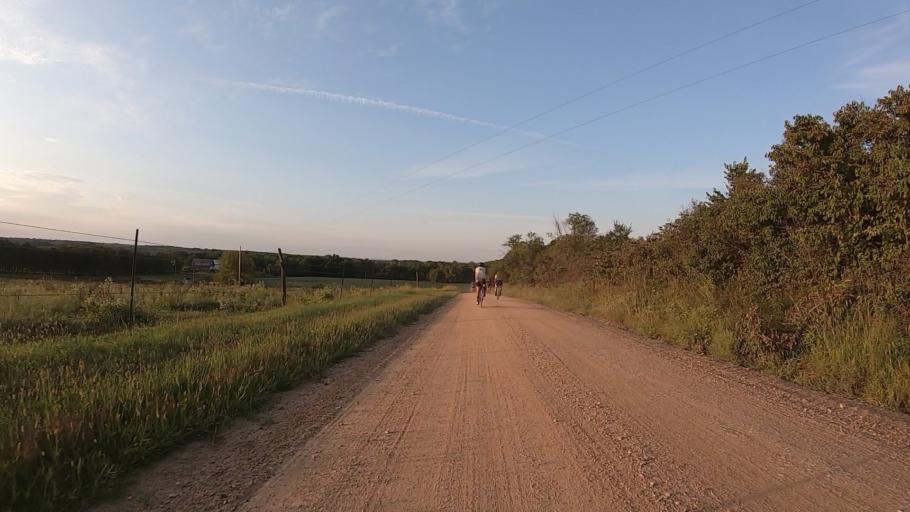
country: US
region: Kansas
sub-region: Marshall County
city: Marysville
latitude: 39.7908
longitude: -96.6837
